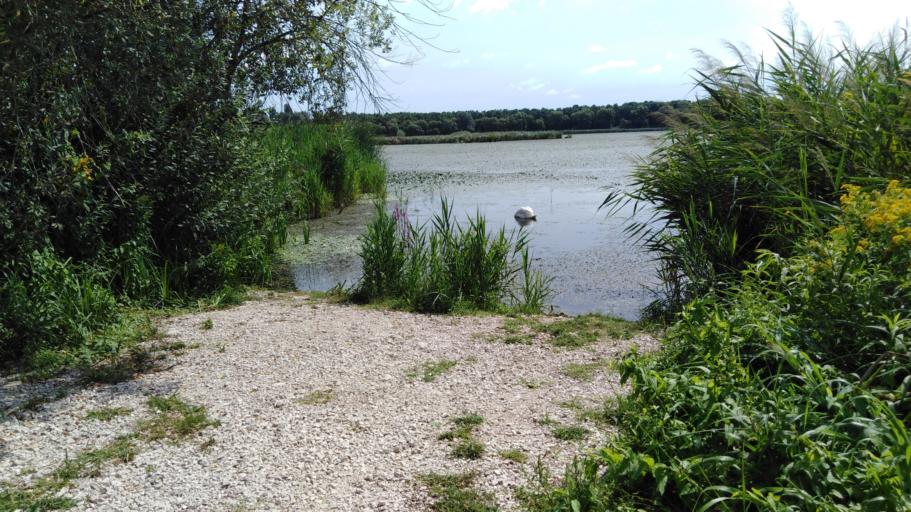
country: HU
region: Zala
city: Zalakomar
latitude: 46.6049
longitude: 17.1666
